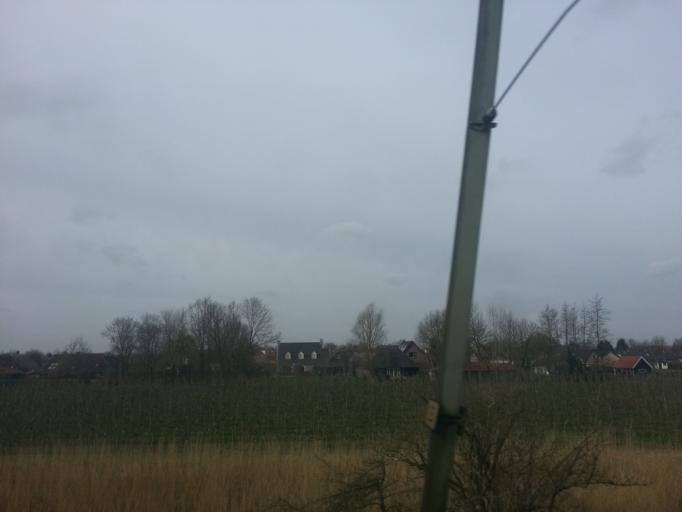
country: NL
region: Gelderland
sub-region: Gemeente Geldermalsen
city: Geldermalsen
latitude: 51.8898
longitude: 5.2684
